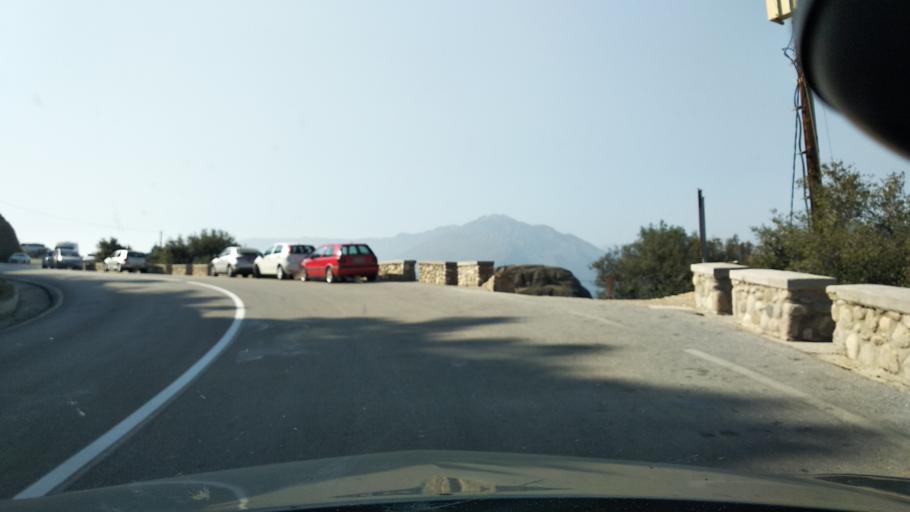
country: GR
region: Thessaly
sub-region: Trikala
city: Kalampaka
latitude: 39.7139
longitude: 21.6387
